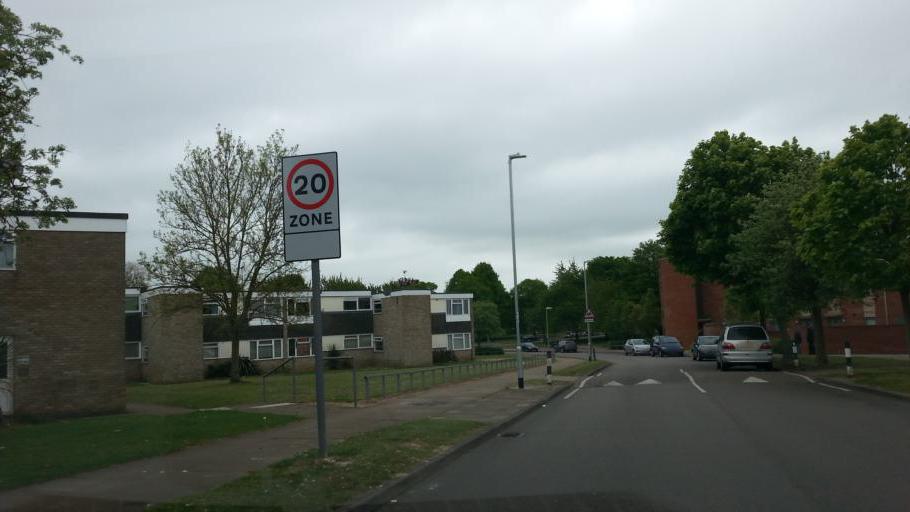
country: GB
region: England
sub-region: Suffolk
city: Bury St Edmunds
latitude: 52.2590
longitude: 0.6960
